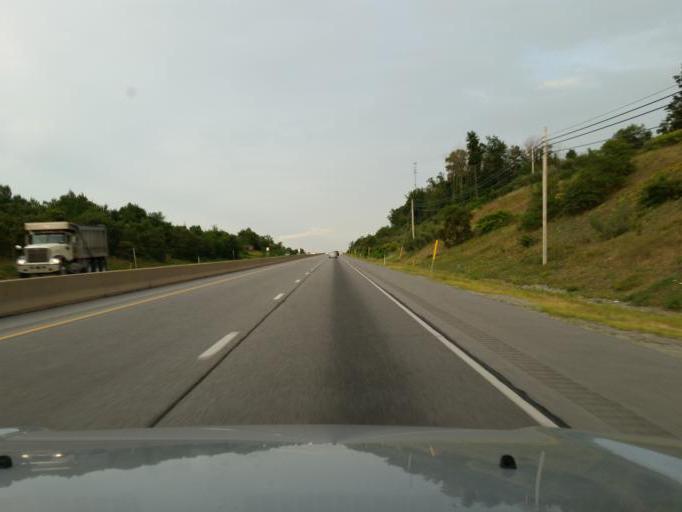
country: US
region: Pennsylvania
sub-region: Indiana County
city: Black Lick
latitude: 40.4503
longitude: -79.1731
